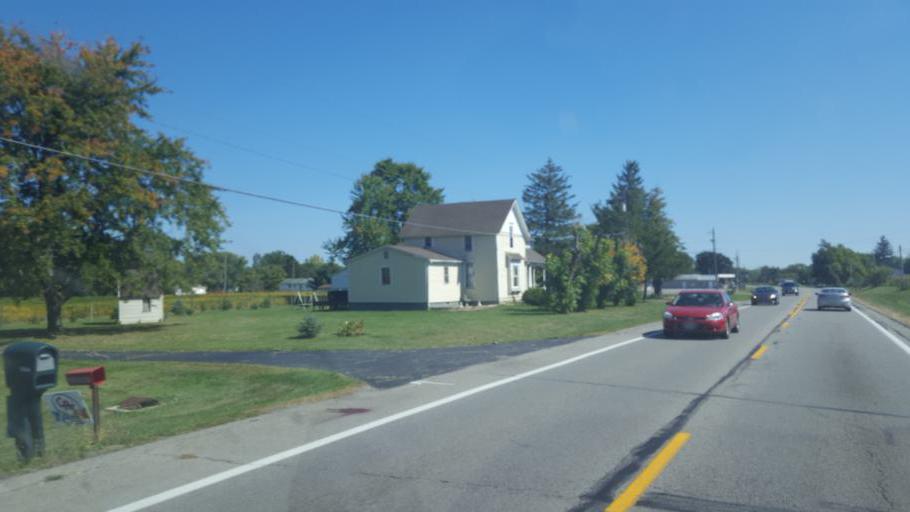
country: US
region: Ohio
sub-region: Morrow County
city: Cardington
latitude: 40.6311
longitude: -82.9736
